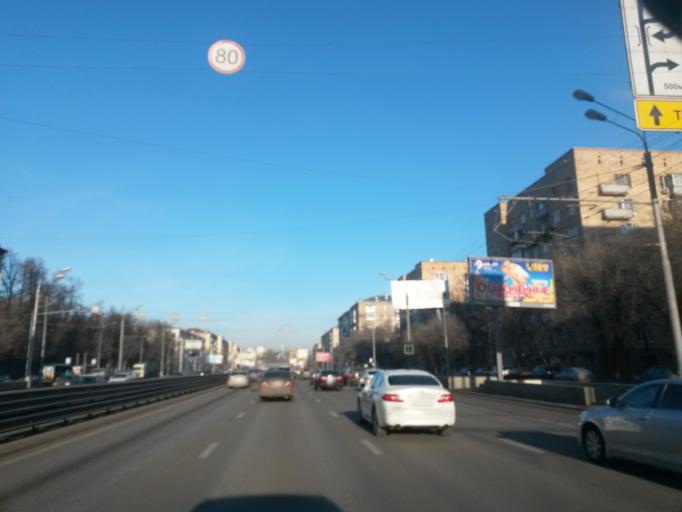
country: RU
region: Moscow
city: Nagornyy
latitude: 55.6564
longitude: 37.6196
